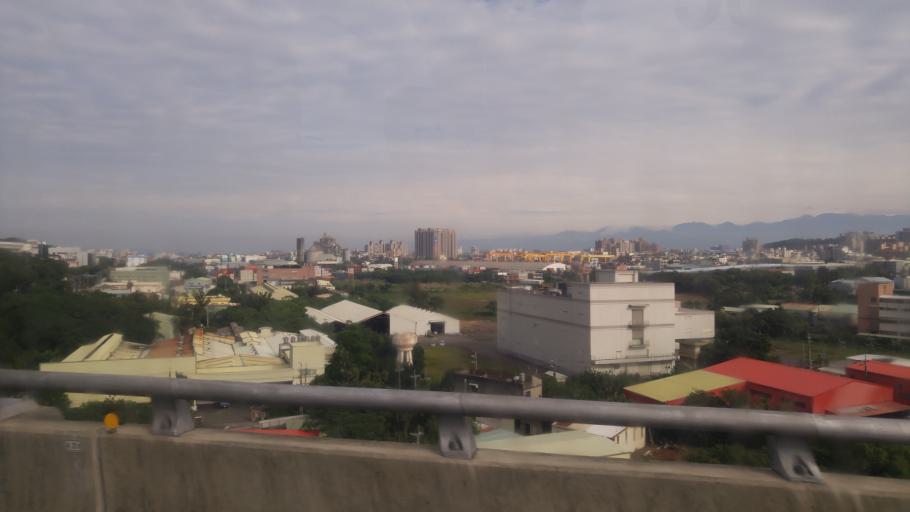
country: TW
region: Taiwan
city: Daxi
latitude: 24.9168
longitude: 121.1674
